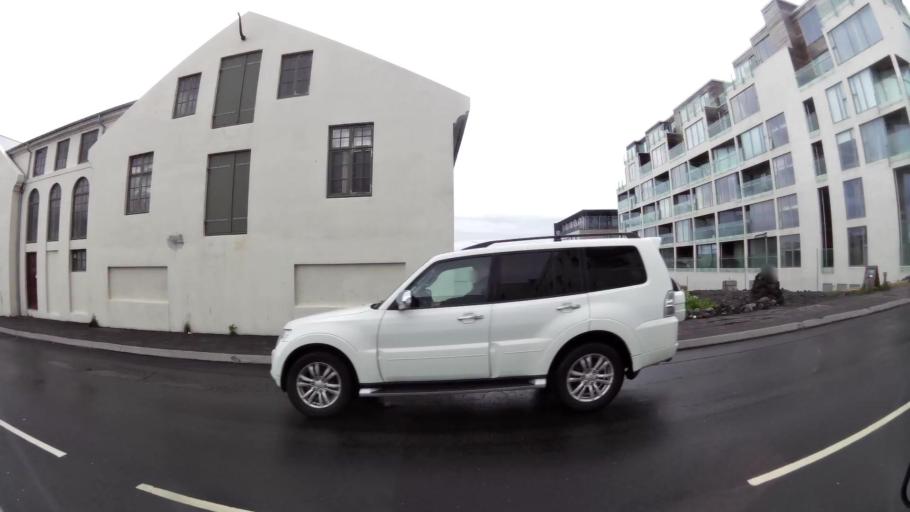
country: IS
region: Capital Region
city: Seltjarnarnes
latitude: 64.1523
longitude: -21.9513
